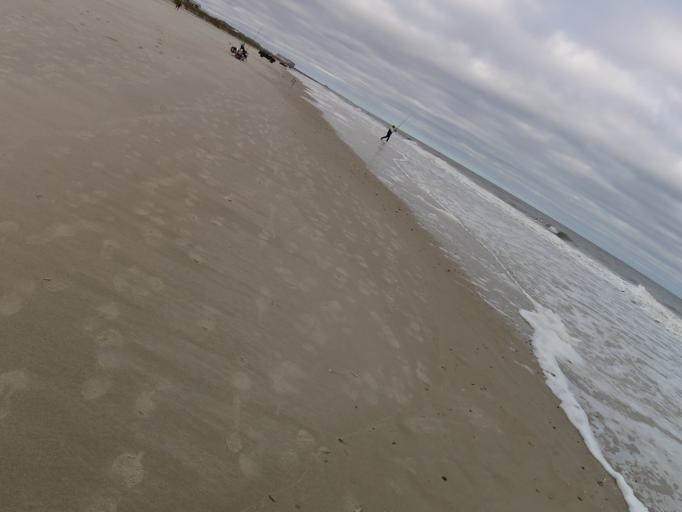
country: US
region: Florida
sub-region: Nassau County
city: Fernandina Beach
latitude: 30.5683
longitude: -81.4428
